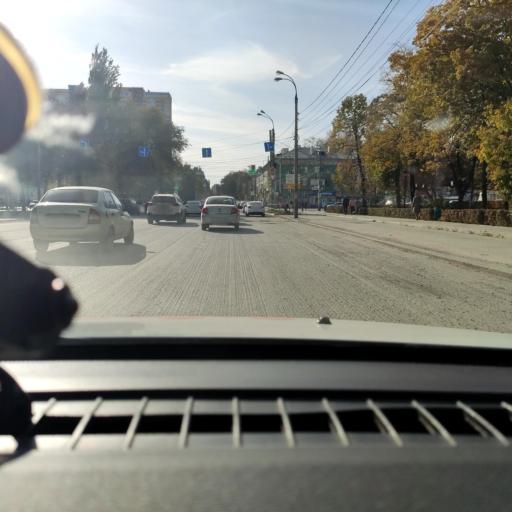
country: RU
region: Samara
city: Samara
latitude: 53.2186
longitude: 50.2658
